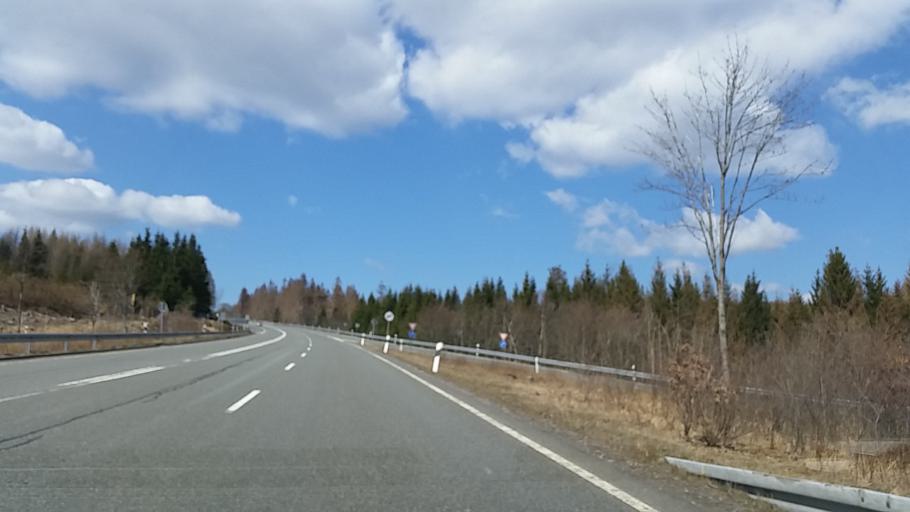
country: DE
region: Lower Saxony
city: Braunlage
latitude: 51.7403
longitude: 10.5881
